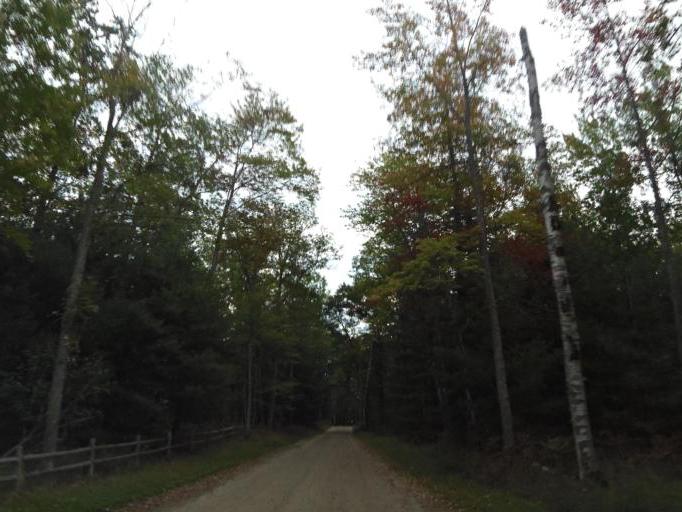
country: US
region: Michigan
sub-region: Roscommon County
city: Saint Helen
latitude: 44.3593
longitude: -84.4711
